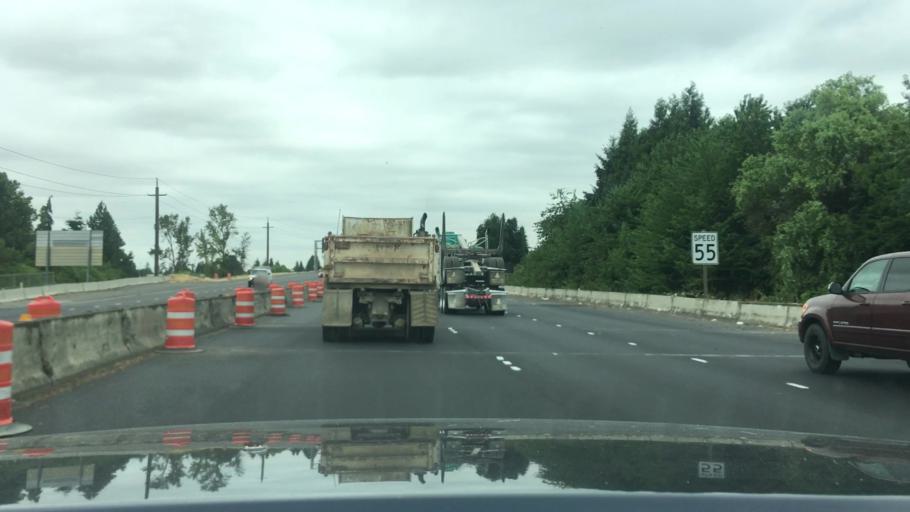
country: US
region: Oregon
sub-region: Lane County
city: Eugene
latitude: 44.0915
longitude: -123.1710
